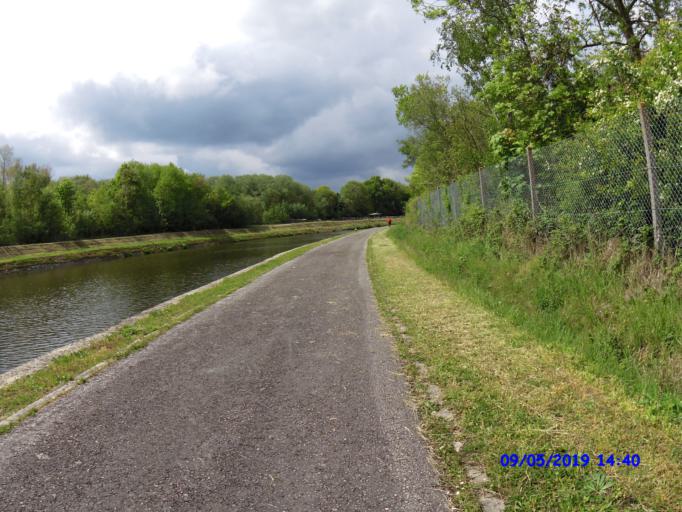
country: BE
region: Wallonia
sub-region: Province du Hainaut
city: Aiseau
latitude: 50.4456
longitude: 4.6138
